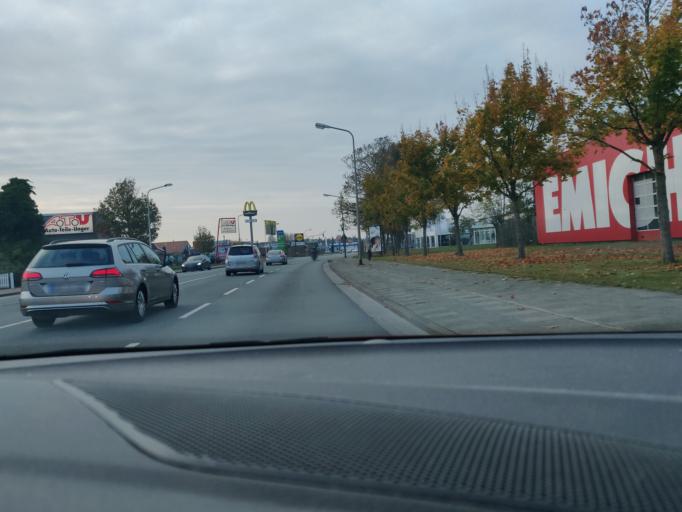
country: DE
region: Lower Saxony
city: Cuxhaven
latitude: 53.8508
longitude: 8.7170
